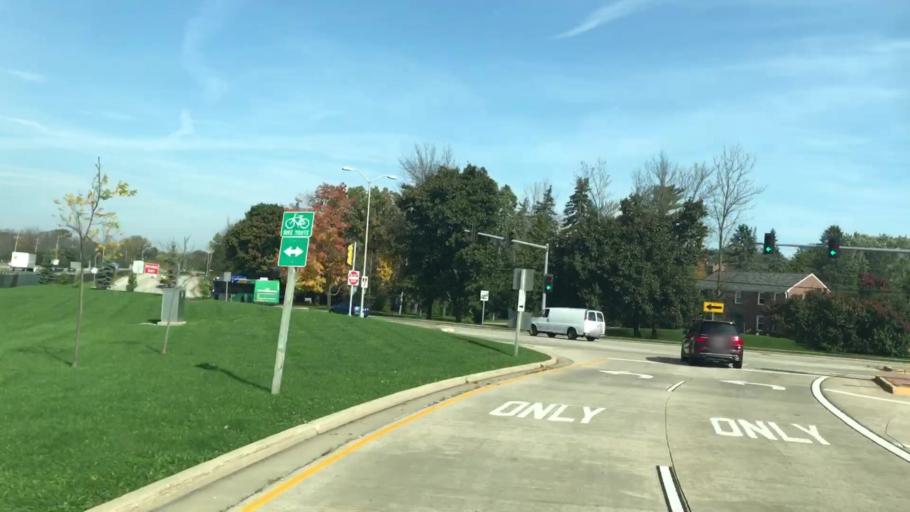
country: US
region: Wisconsin
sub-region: Milwaukee County
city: River Hills
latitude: 43.1865
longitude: -87.9216
